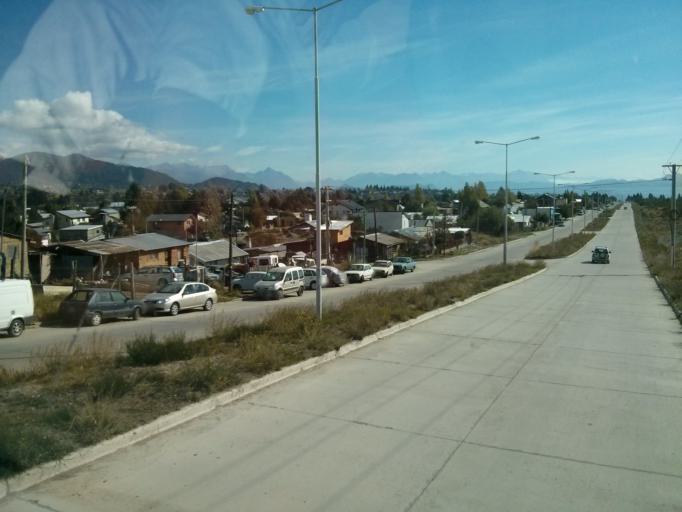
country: AR
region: Rio Negro
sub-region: Departamento de Bariloche
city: San Carlos de Bariloche
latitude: -41.1461
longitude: -71.2679
